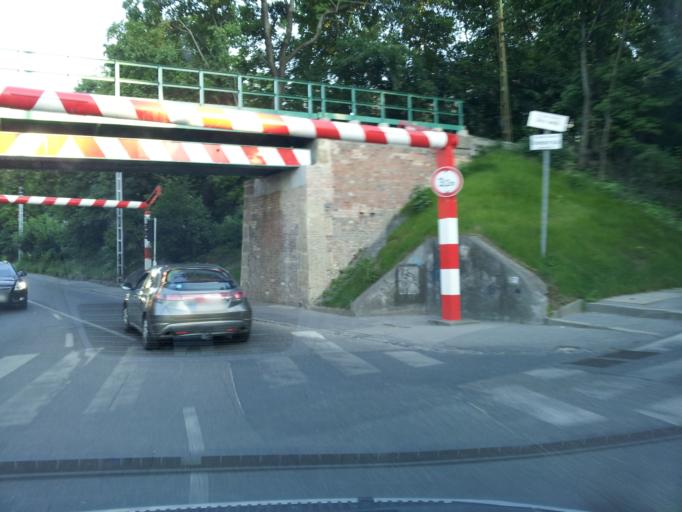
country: HU
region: Budapest
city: Budapest XII. keruelet
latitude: 47.5091
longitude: 19.0092
